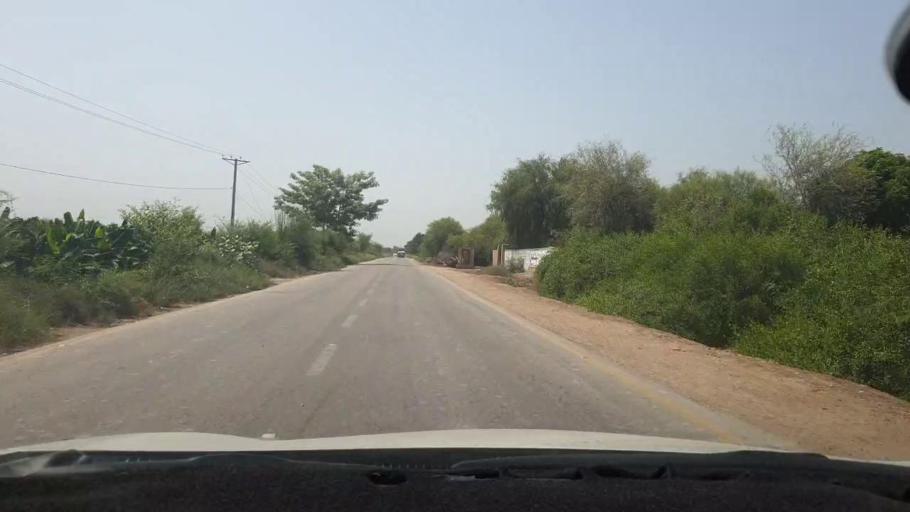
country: PK
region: Sindh
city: Bhit Shah
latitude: 25.8620
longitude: 68.5142
